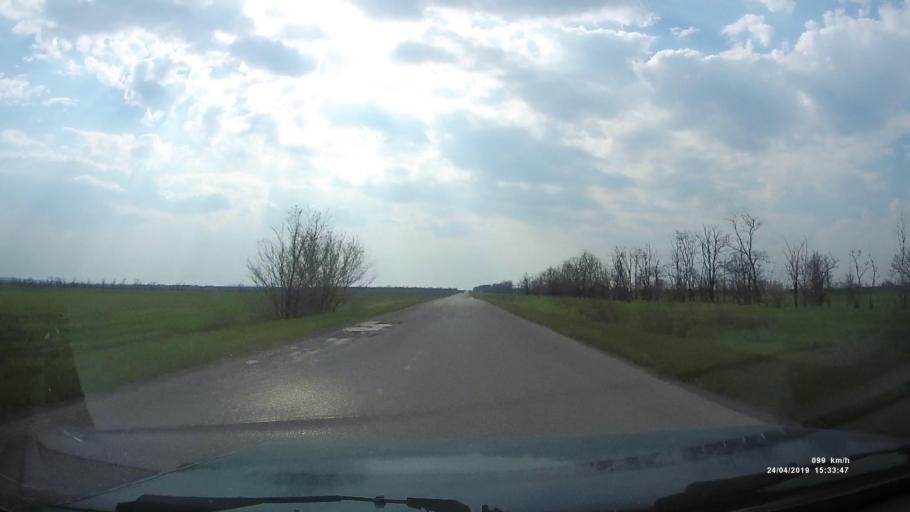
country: RU
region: Kalmykiya
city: Yashalta
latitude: 46.5991
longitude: 42.9307
